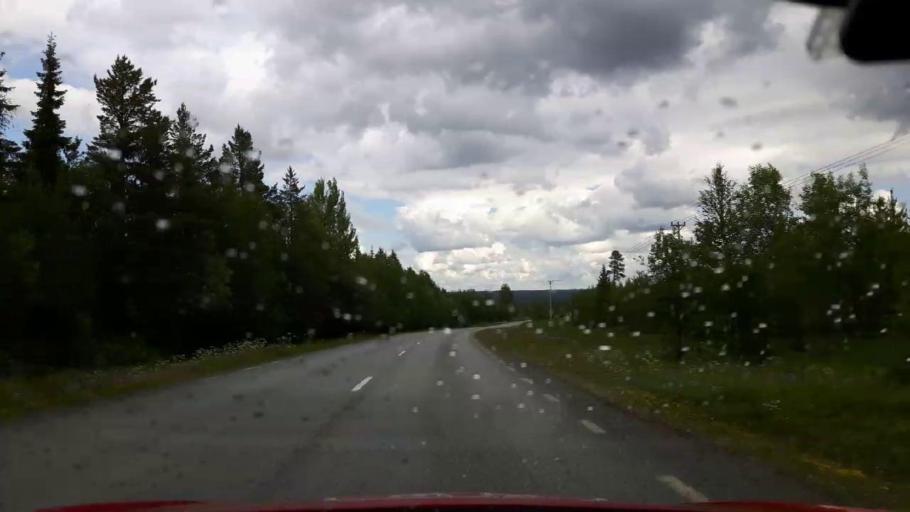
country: SE
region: Jaemtland
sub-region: Krokoms Kommun
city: Krokom
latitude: 63.5391
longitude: 14.2578
